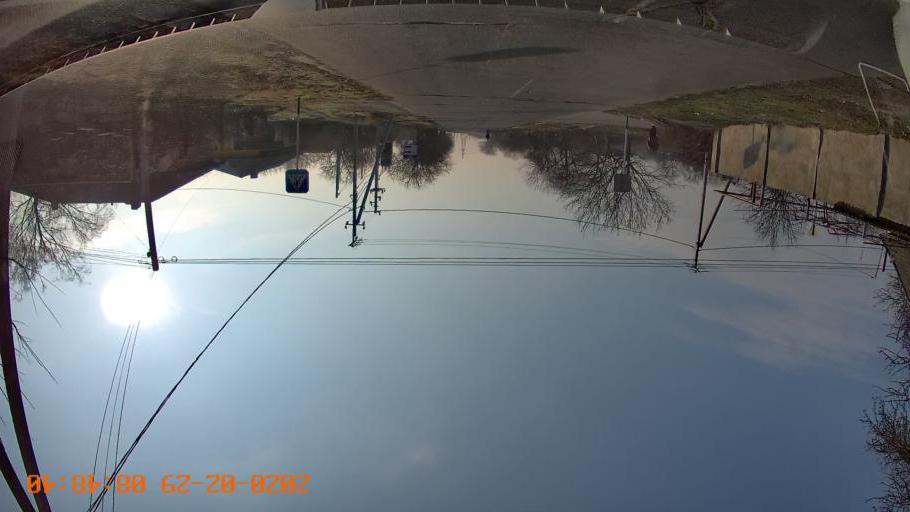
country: MD
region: Anenii Noi
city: Varnita
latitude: 46.9200
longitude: 29.4857
